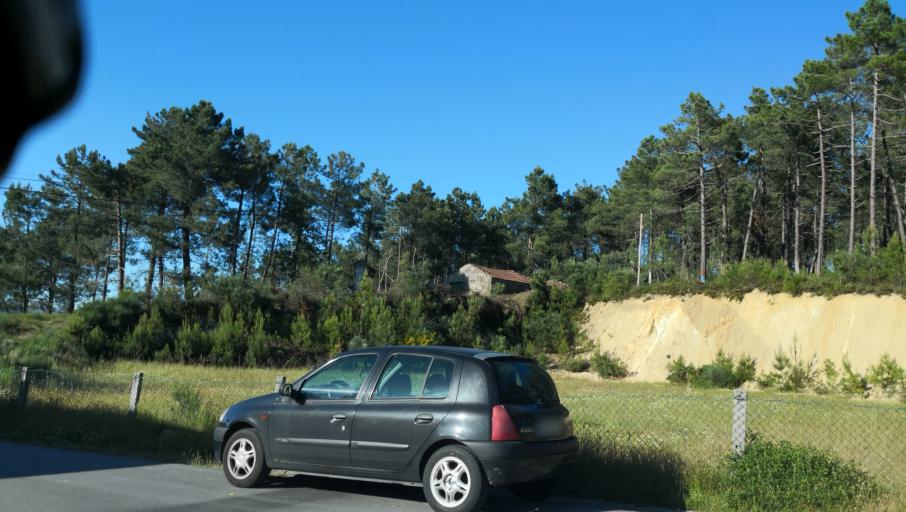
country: PT
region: Vila Real
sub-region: Vila Real
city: Vila Real
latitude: 41.3208
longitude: -7.6757
